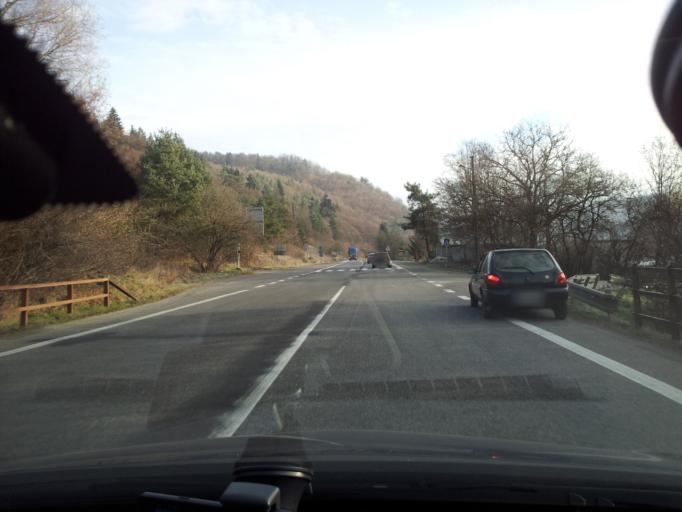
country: SK
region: Banskobystricky
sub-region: Okres Banska Bystrica
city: Banska Bystrica
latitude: 48.7433
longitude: 19.2164
